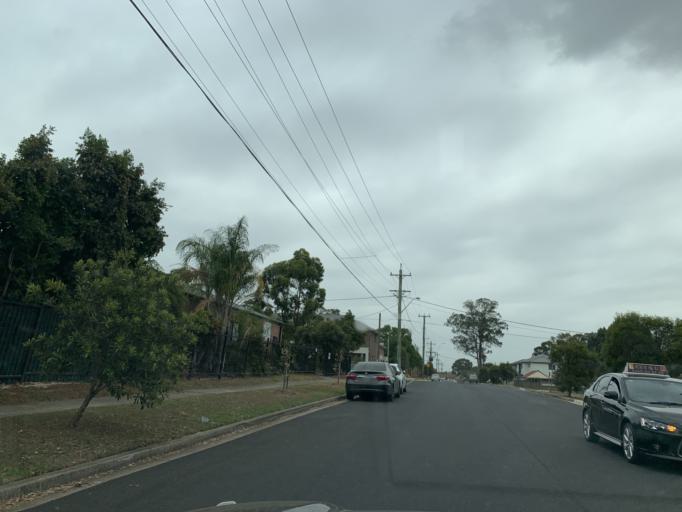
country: AU
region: New South Wales
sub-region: Blacktown
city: Doonside
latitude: -33.7645
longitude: 150.8892
